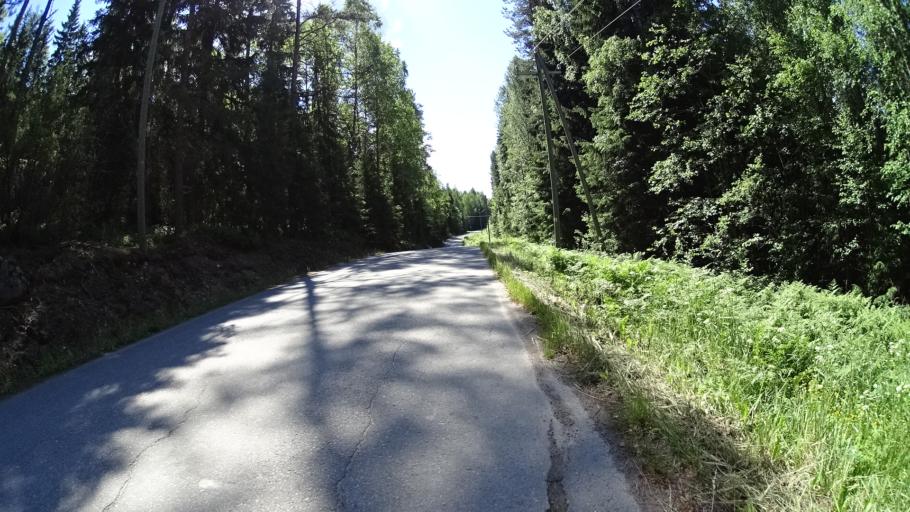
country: FI
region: Uusimaa
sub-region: Helsinki
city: Vihti
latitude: 60.3077
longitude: 24.4390
